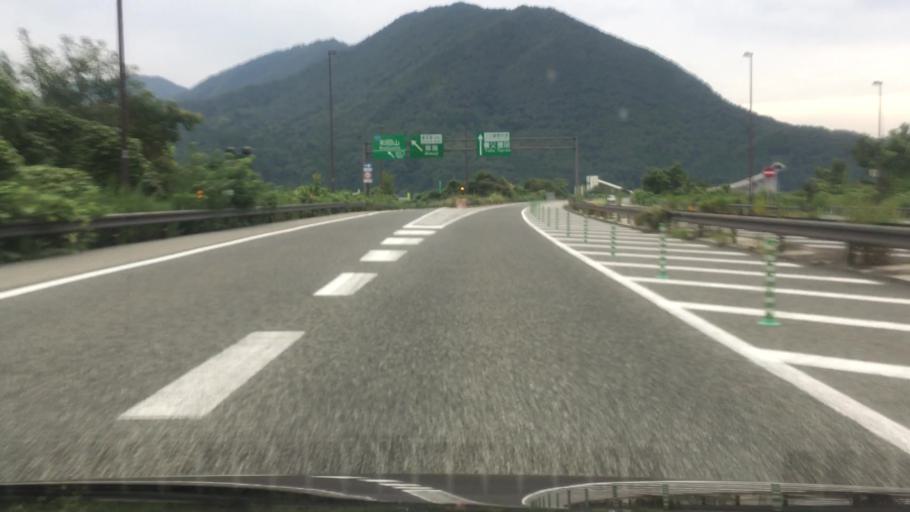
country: JP
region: Hyogo
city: Toyooka
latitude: 35.3126
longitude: 134.8499
